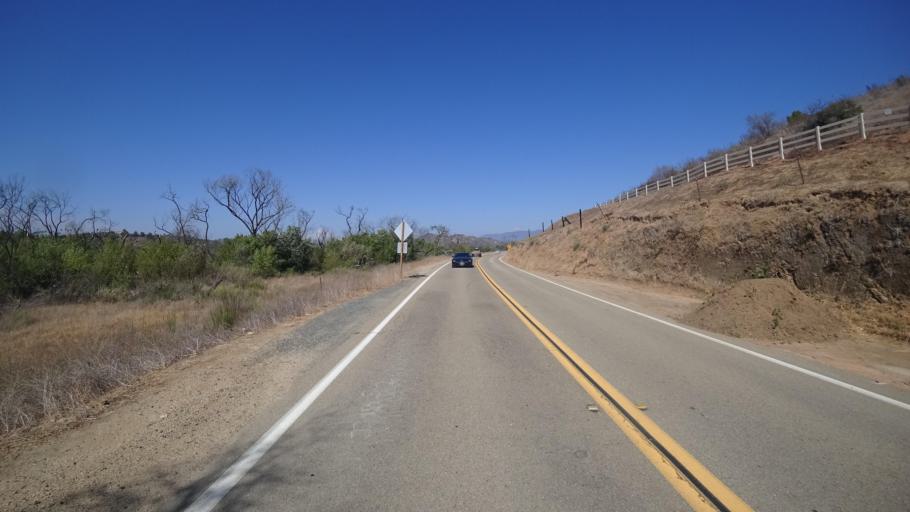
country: US
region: California
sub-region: San Diego County
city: Bonsall
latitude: 33.2973
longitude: -117.2132
